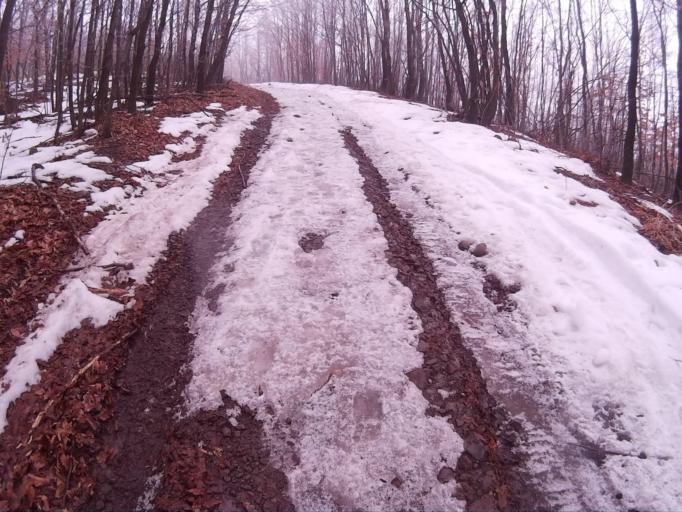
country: HU
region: Heves
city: Domoszlo
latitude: 47.8832
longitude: 20.0880
